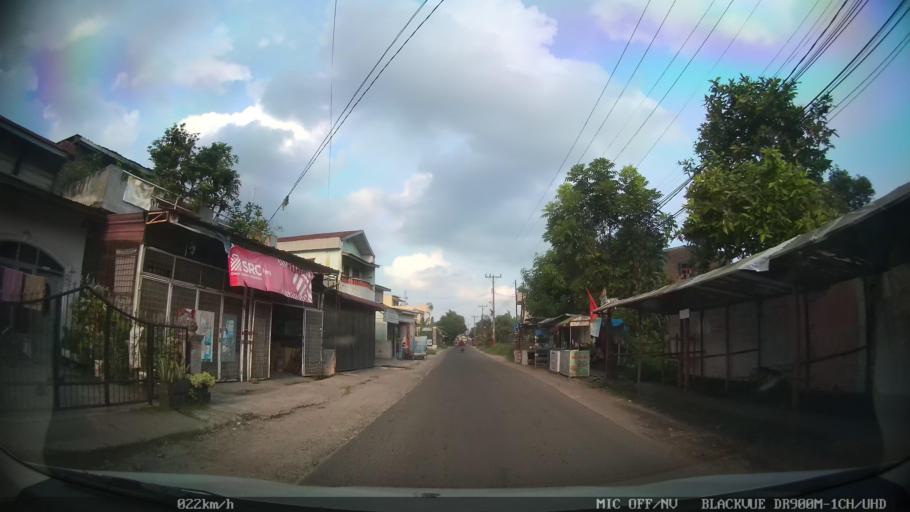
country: ID
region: North Sumatra
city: Medan
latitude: 3.5851
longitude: 98.7338
